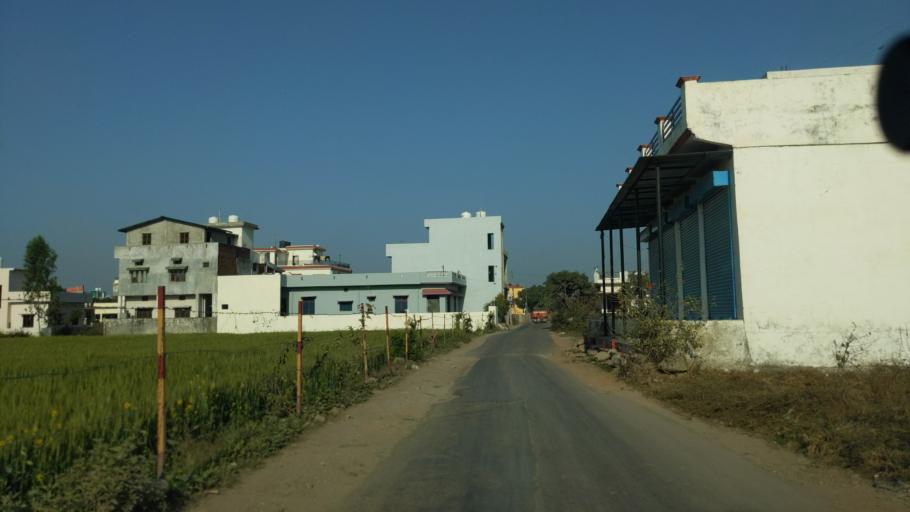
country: IN
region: Uttarakhand
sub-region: Naini Tal
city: Haldwani
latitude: 29.2097
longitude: 79.4920
